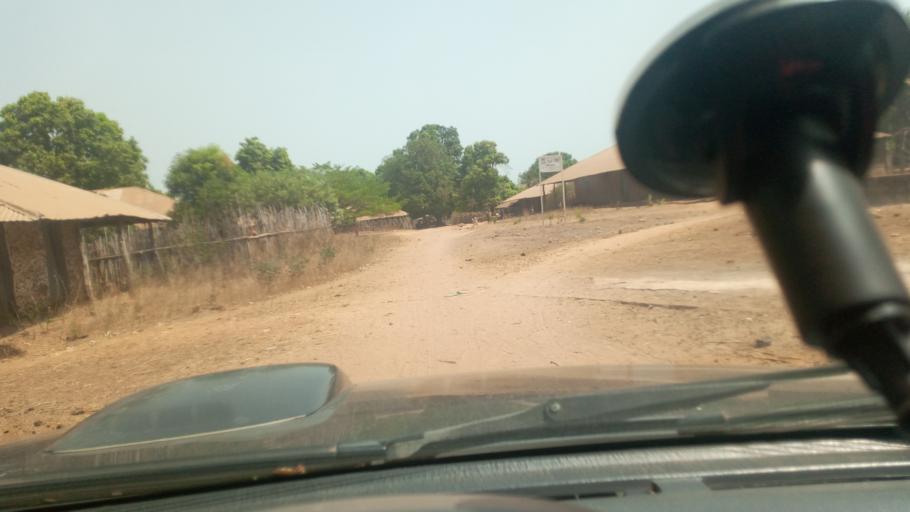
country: SN
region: Sedhiou
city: Sedhiou
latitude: 12.4437
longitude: -15.6163
